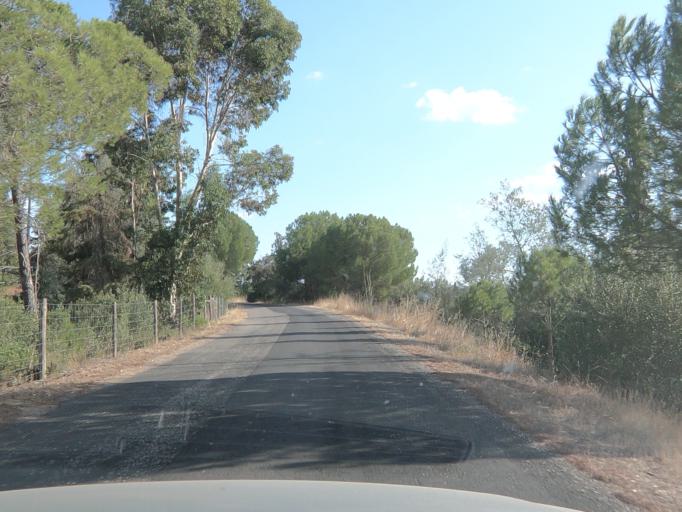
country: PT
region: Setubal
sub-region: Alcacer do Sal
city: Alcacer do Sal
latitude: 38.2505
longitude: -8.2974
